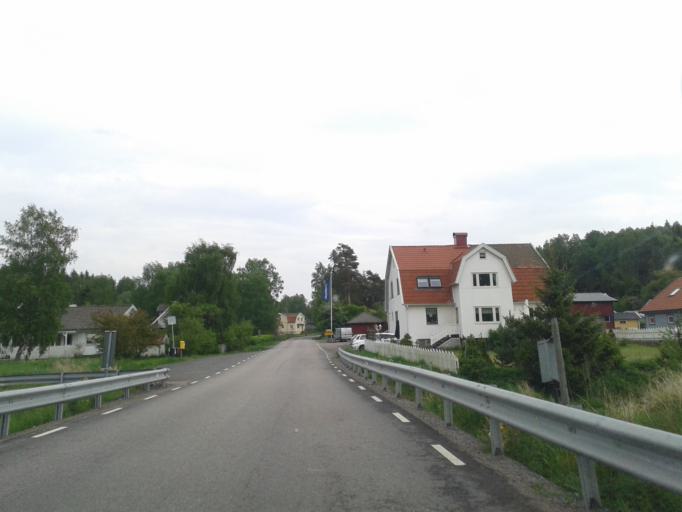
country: SE
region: Vaestra Goetaland
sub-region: Kungalvs Kommun
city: Kode
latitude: 57.9032
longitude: 11.8992
